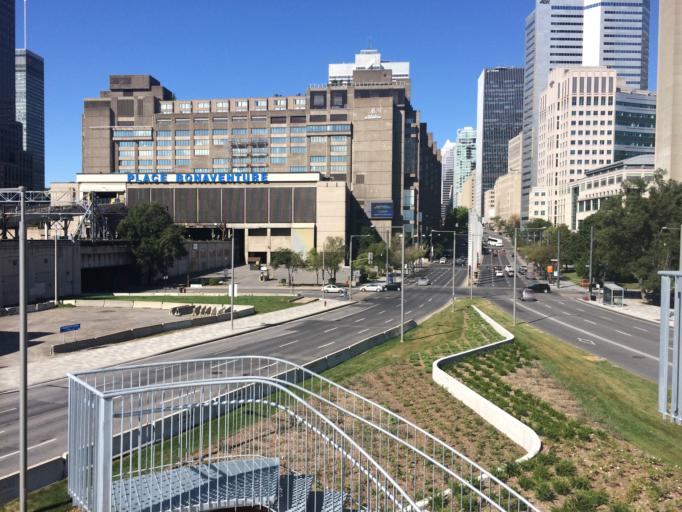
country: CA
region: Quebec
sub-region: Montreal
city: Montreal
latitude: 45.4984
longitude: -73.5616
